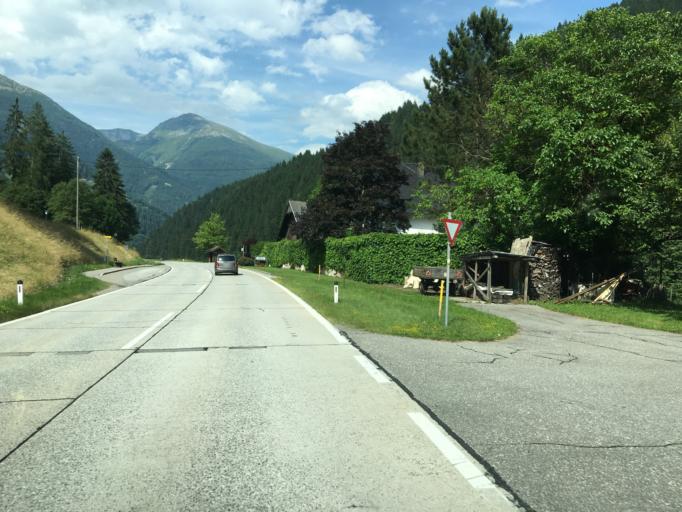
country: AT
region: Carinthia
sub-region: Politischer Bezirk Spittal an der Drau
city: Stall
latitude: 46.9176
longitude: 13.0735
